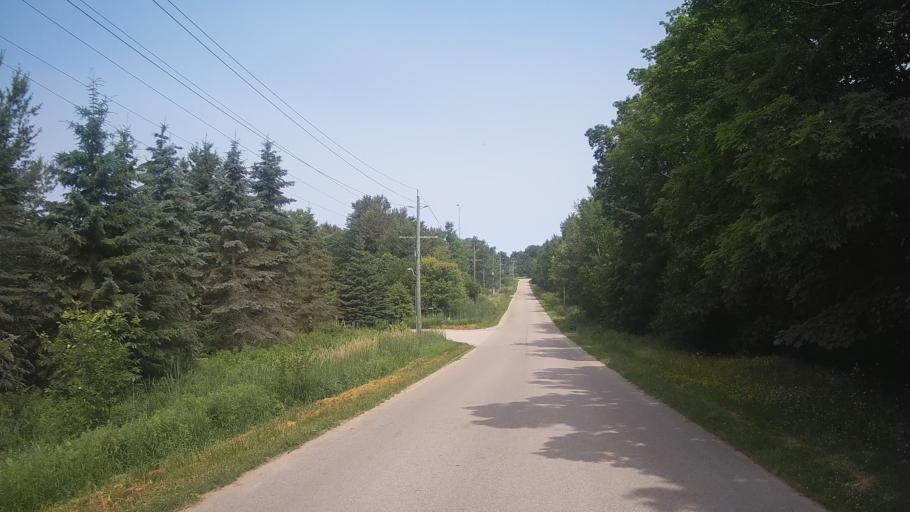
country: CA
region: Ontario
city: Barrie
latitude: 44.4550
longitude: -79.6298
